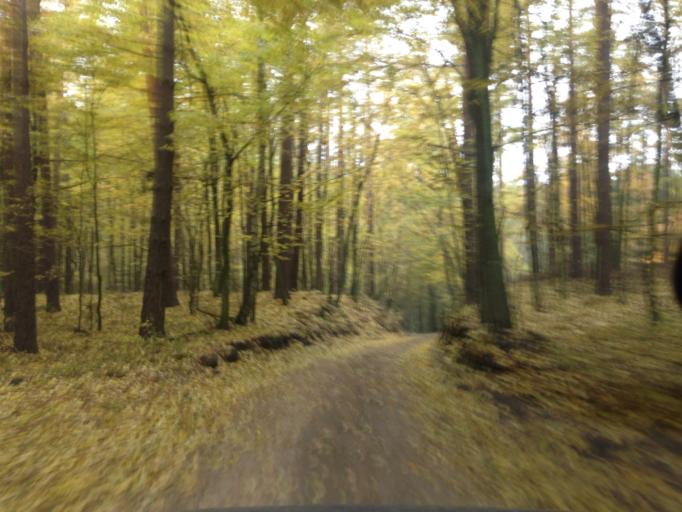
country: PL
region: Kujawsko-Pomorskie
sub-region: Powiat brodnicki
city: Gorzno
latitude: 53.2159
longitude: 19.6956
